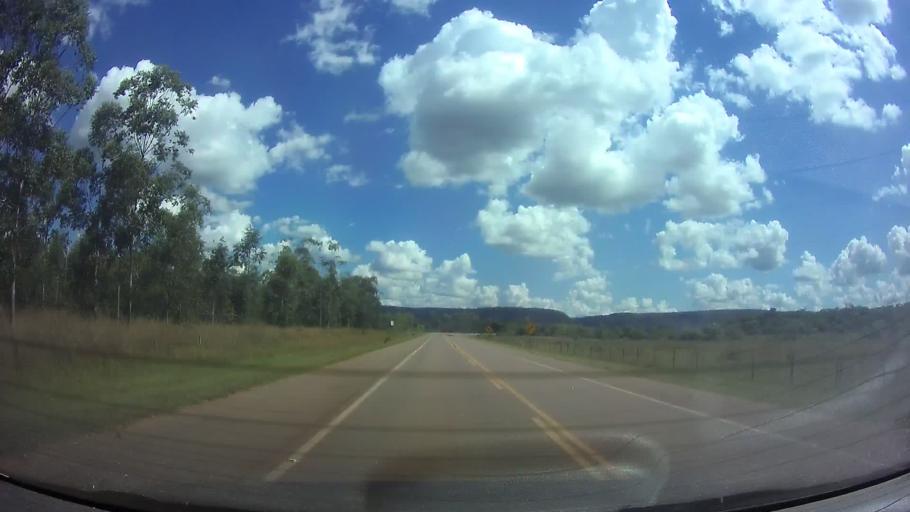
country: PY
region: Guaira
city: Itape
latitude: -25.9062
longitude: -56.6744
